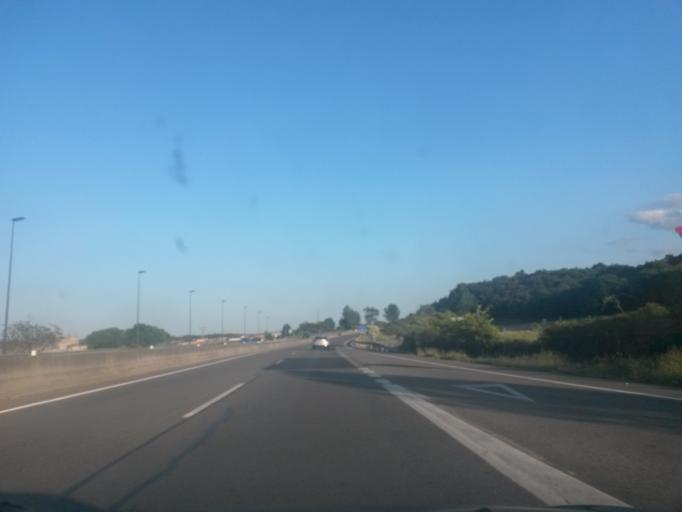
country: ES
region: Catalonia
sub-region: Provincia de Girona
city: Cornella del Terri
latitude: 42.0909
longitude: 2.8077
